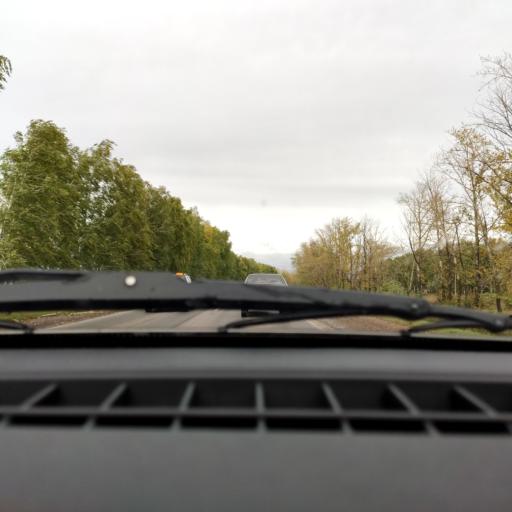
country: RU
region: Bashkortostan
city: Davlekanovo
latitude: 54.2307
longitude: 55.0114
